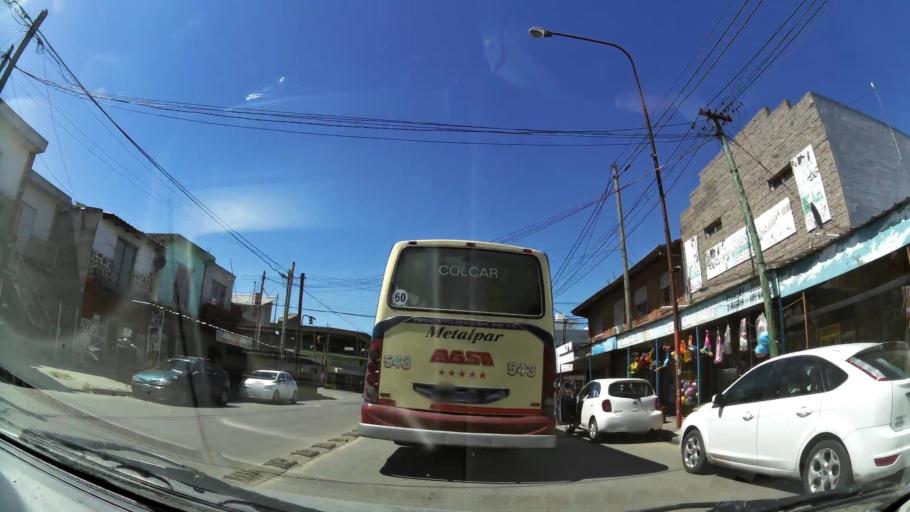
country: AR
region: Buenos Aires
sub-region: Partido de Quilmes
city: Quilmes
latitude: -34.7305
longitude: -58.3039
